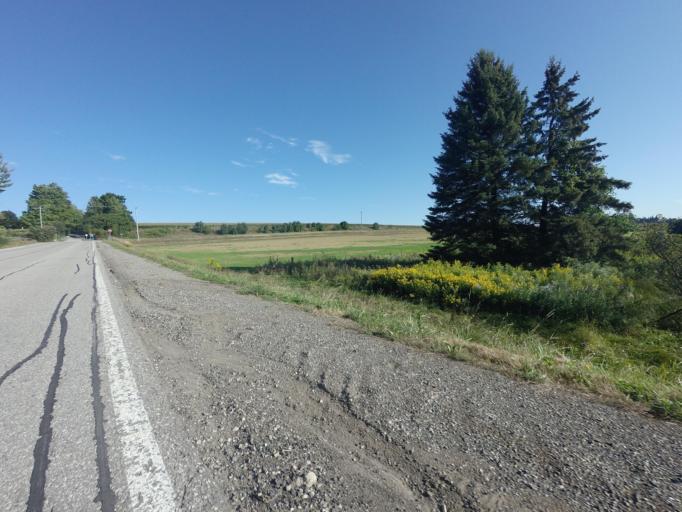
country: CA
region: Ontario
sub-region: Wellington County
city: Guelph
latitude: 43.6520
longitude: -80.4175
